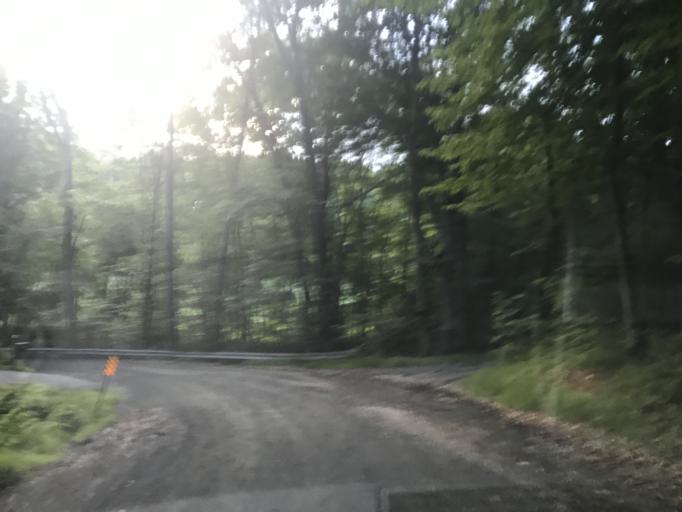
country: US
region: Maryland
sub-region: Harford County
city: Bel Air South
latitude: 39.5034
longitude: -76.2834
